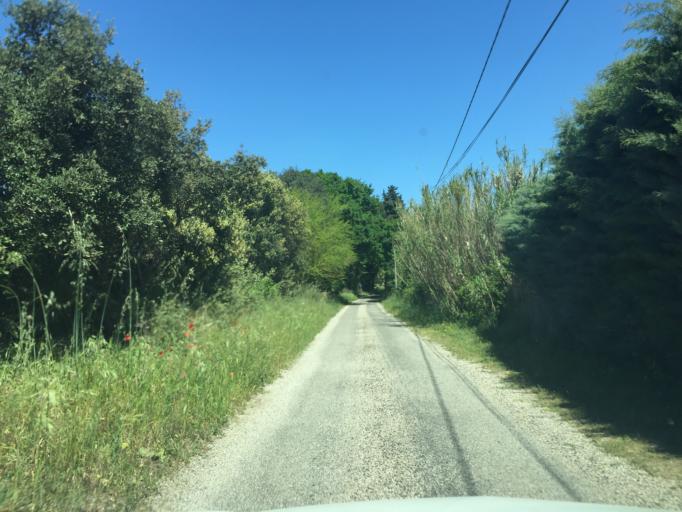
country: FR
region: Provence-Alpes-Cote d'Azur
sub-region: Departement du Vaucluse
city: Caderousse
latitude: 44.1005
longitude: 4.7952
